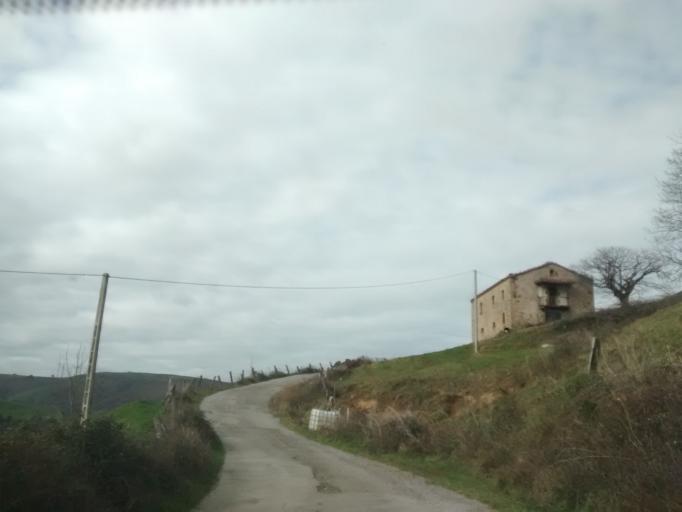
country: ES
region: Cantabria
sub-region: Provincia de Cantabria
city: Lierganes
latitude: 43.3248
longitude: -3.7328
